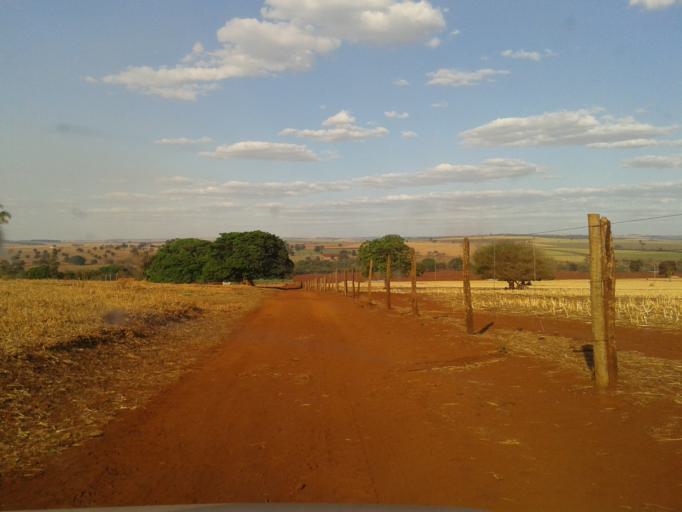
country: BR
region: Minas Gerais
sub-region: Capinopolis
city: Capinopolis
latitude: -18.6844
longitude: -49.3815
